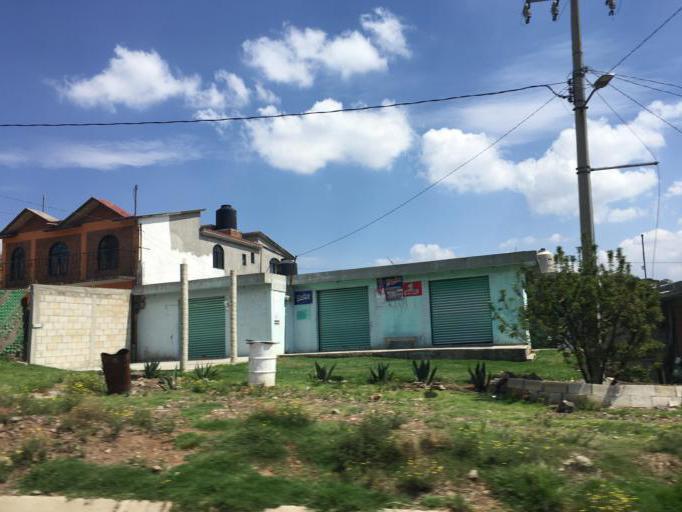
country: MX
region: Mexico
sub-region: Timilpan
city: Tercera Manzana de Zaragoza
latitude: 19.8844
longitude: -99.6534
